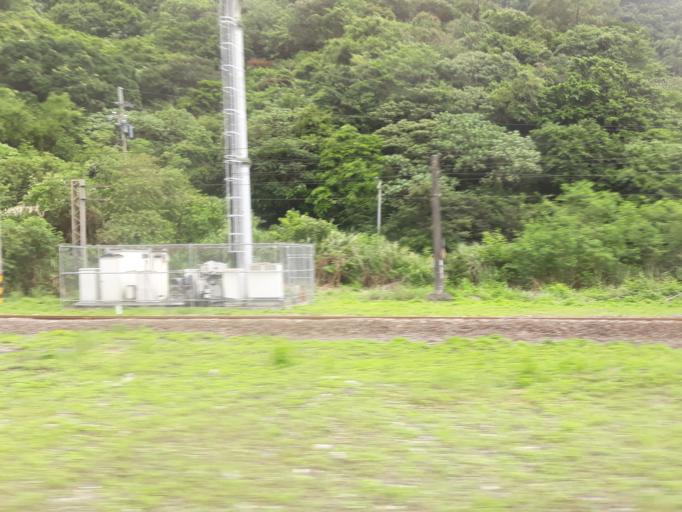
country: TW
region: Taiwan
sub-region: Yilan
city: Yilan
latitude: 24.5650
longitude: 121.8429
